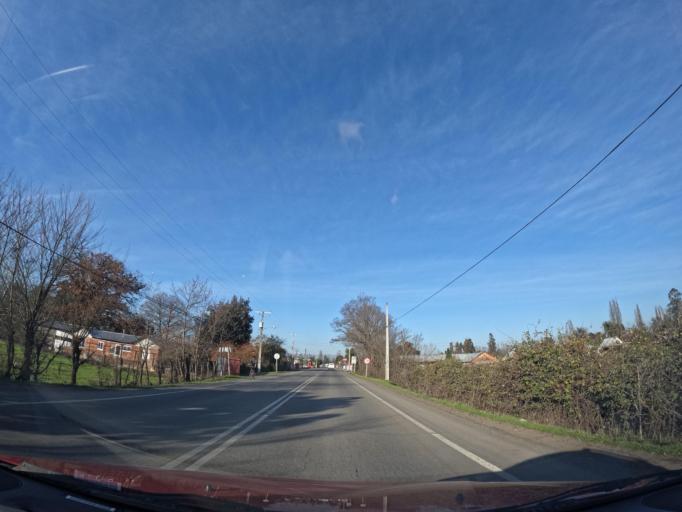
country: CL
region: Maule
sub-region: Provincia de Talca
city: San Clemente
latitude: -35.6224
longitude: -71.4899
